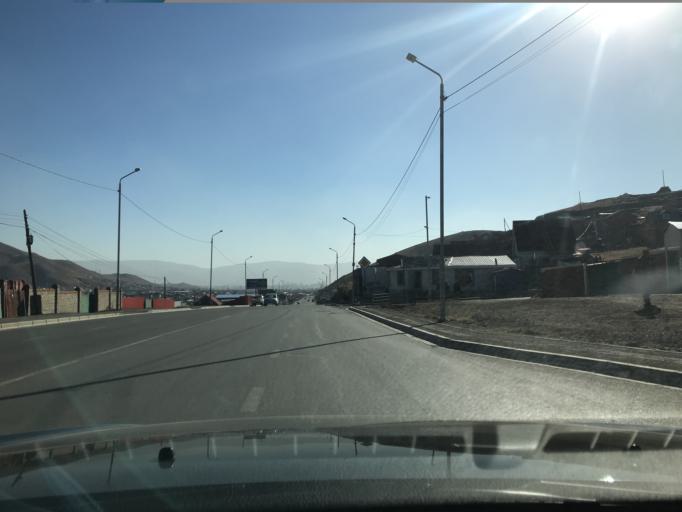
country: MN
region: Ulaanbaatar
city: Ulaanbaatar
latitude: 47.9935
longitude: 106.9257
